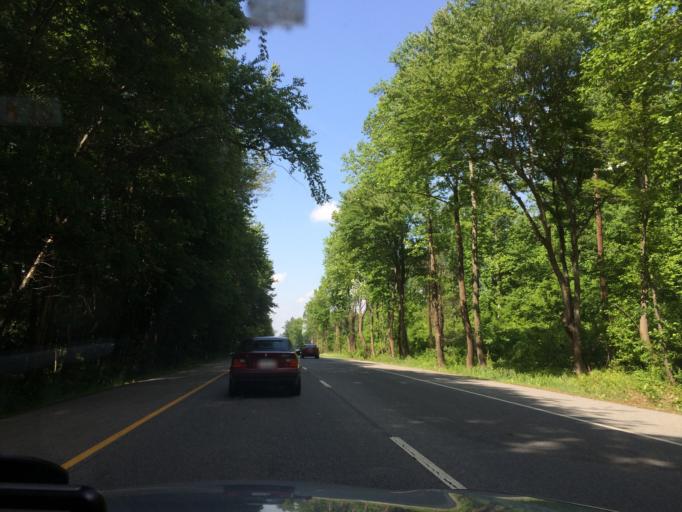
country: US
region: Maryland
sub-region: Prince George's County
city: Bowie
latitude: 38.9753
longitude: -76.7144
